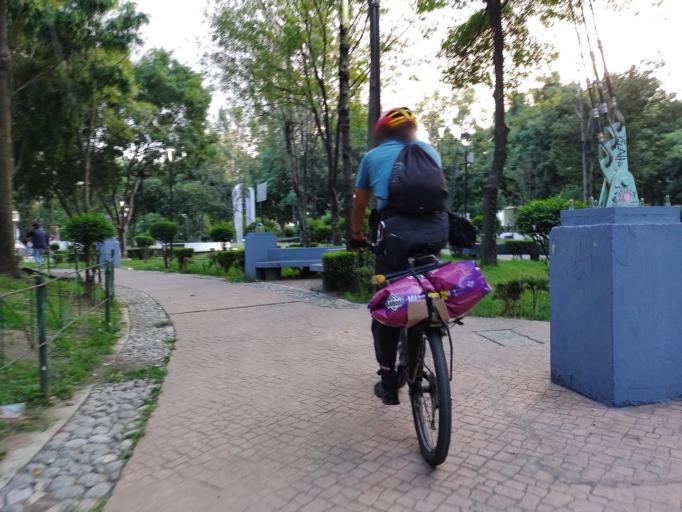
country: MX
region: Mexico City
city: Cuauhtemoc
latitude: 19.4533
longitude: -99.1432
